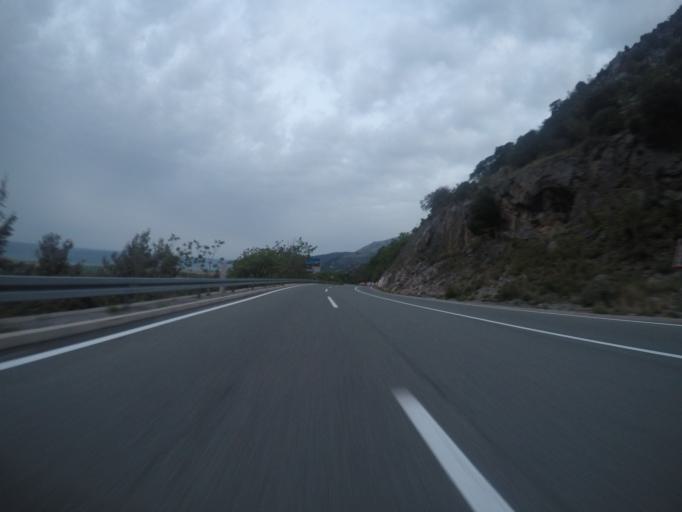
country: ME
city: Petrovac na Moru
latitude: 42.1905
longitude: 18.9881
